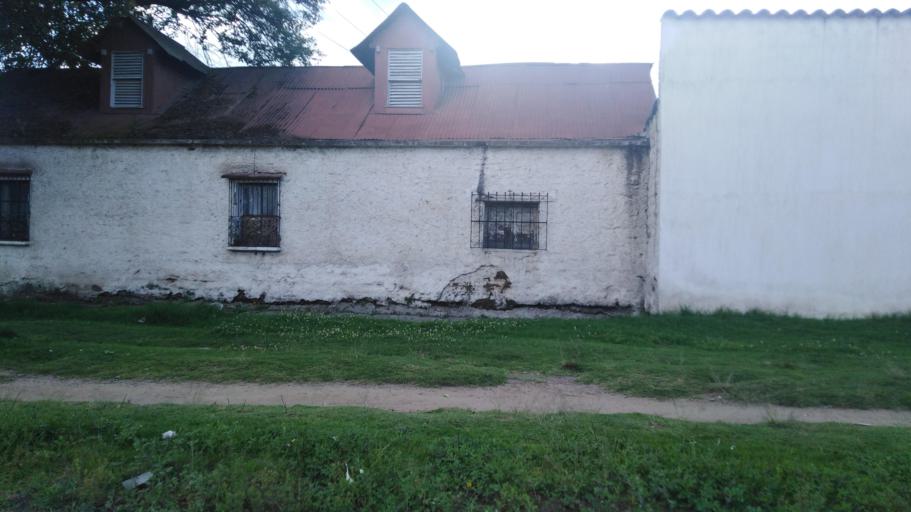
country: GT
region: Quetzaltenango
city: Olintepeque
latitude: 14.8633
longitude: -91.5124
